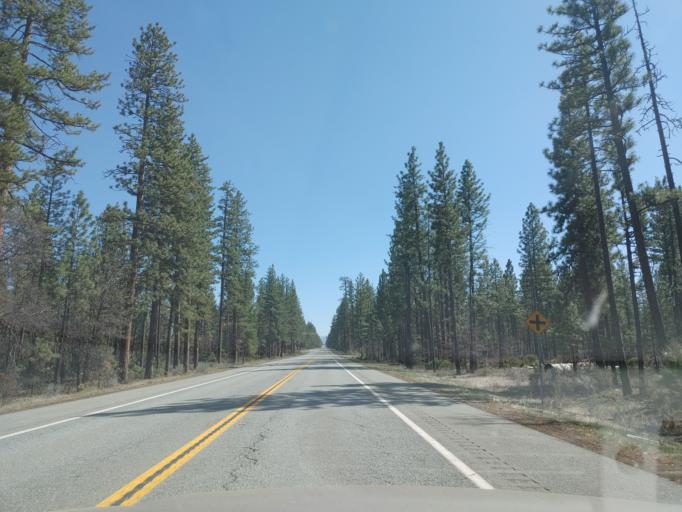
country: US
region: California
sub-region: Shasta County
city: Burney
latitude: 40.9929
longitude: -121.6280
